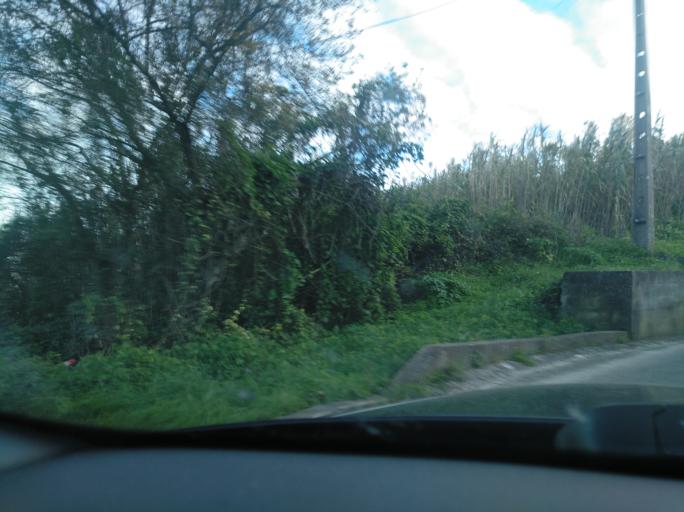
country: PT
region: Lisbon
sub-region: Loures
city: Unhos
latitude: 38.8235
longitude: -9.1261
